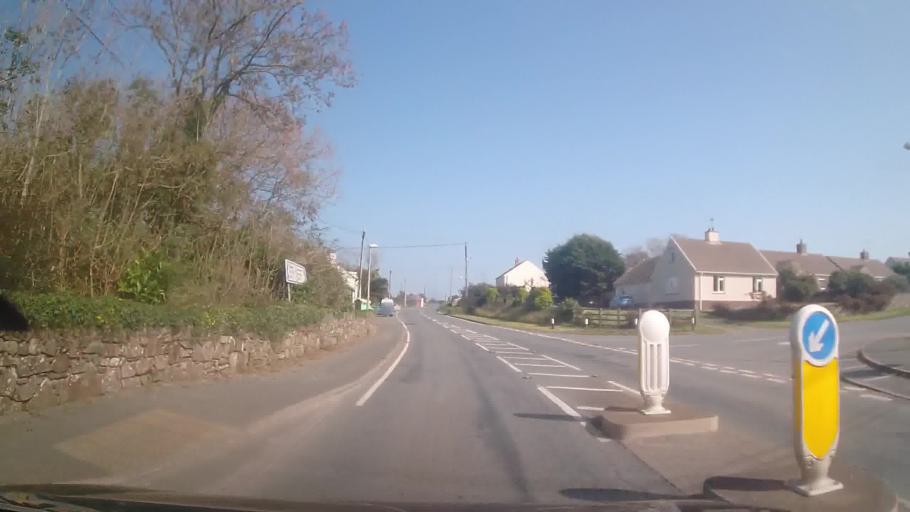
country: GB
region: Wales
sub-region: Pembrokeshire
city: Llanrhian
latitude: 51.9285
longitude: -5.1593
